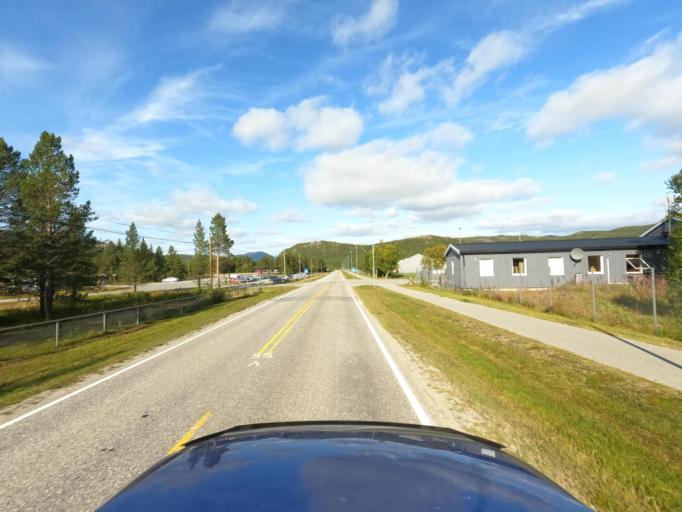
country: NO
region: Finnmark Fylke
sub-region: Porsanger
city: Lakselv
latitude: 69.9031
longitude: 24.9997
